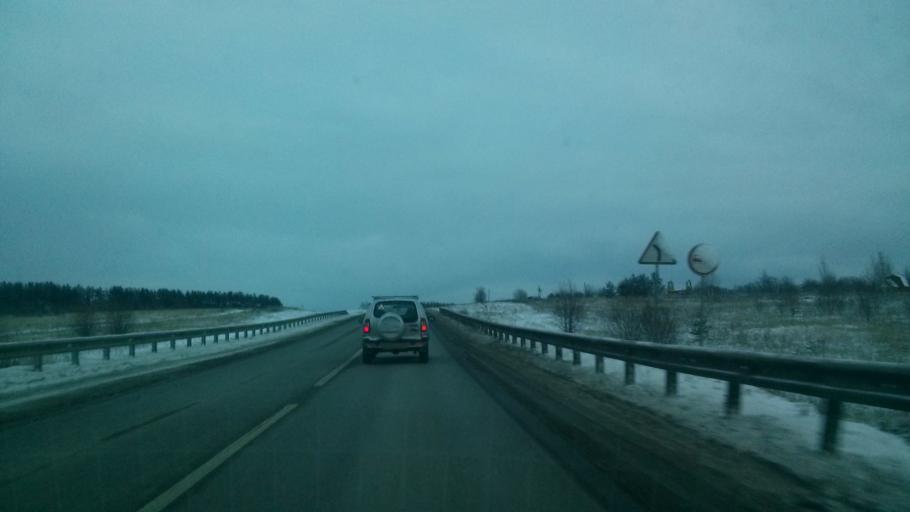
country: RU
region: Nizjnij Novgorod
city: Bogorodsk
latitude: 56.0874
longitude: 43.5527
